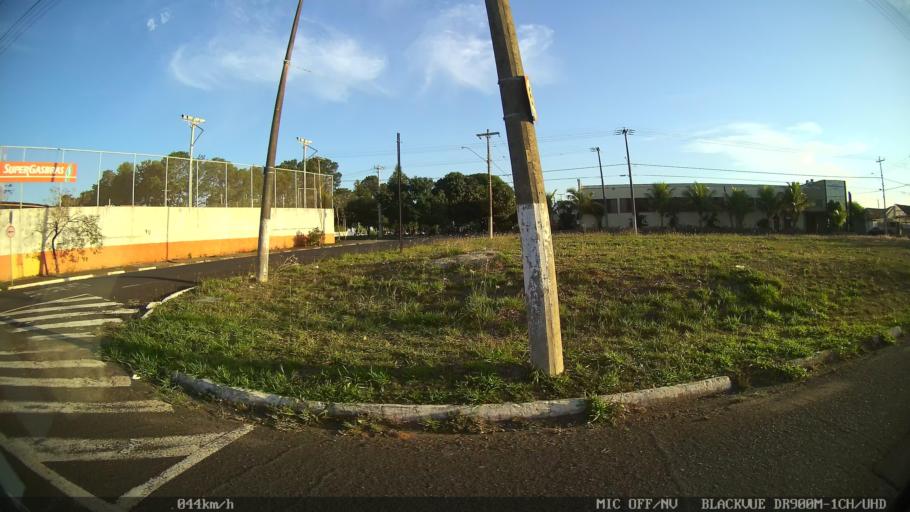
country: BR
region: Sao Paulo
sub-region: Franca
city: Franca
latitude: -20.5134
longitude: -47.3828
